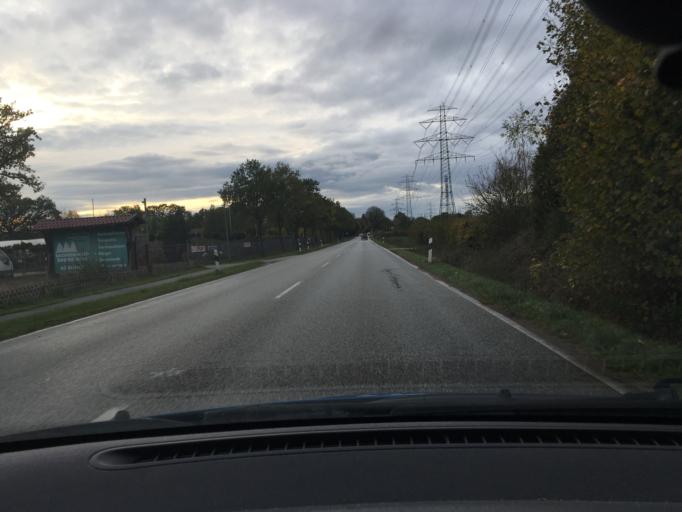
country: DE
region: Schleswig-Holstein
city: Bornsen
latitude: 53.4871
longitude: 10.2977
